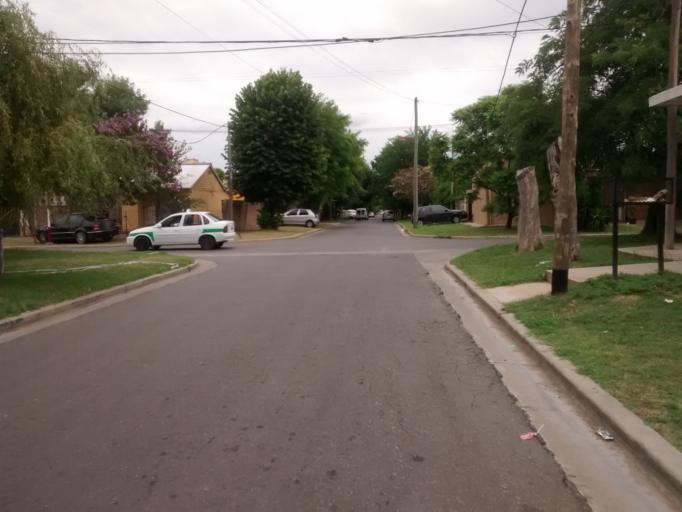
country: AR
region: Buenos Aires
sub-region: Partido de La Plata
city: La Plata
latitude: -34.9419
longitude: -57.9291
